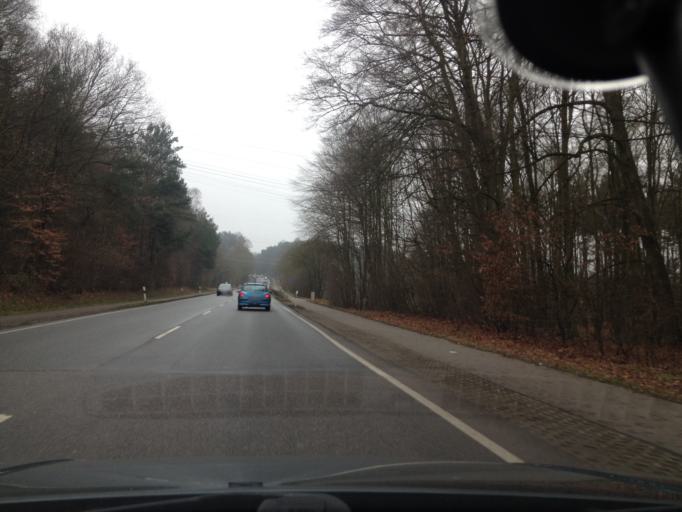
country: DE
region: Saarland
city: Homburg
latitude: 49.3024
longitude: 7.3281
